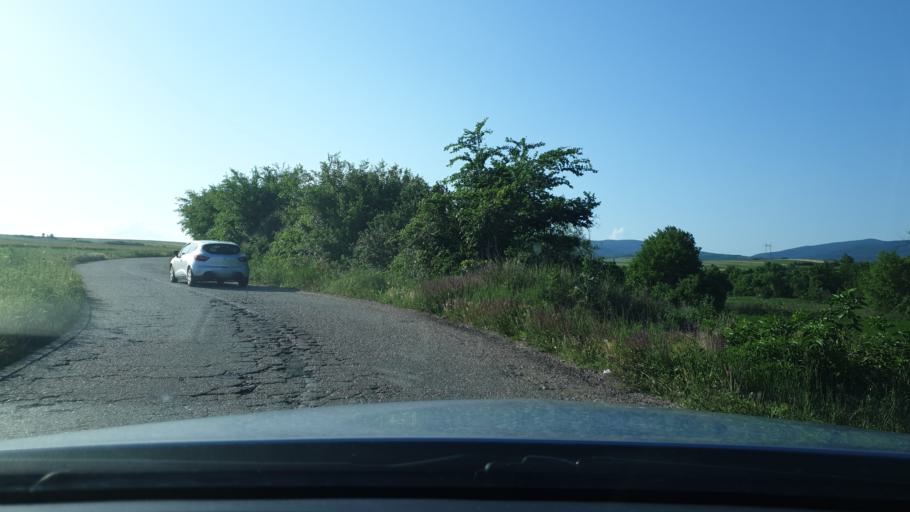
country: RS
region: Central Serbia
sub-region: Nisavski Okrug
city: Aleksinac
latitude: 43.6145
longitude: 21.6856
